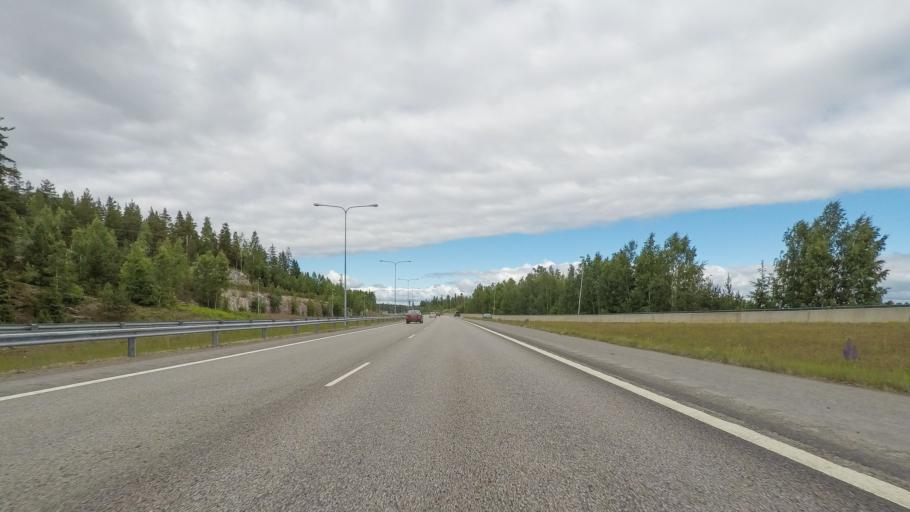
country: FI
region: Paijanne Tavastia
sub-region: Lahti
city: Heinola
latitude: 61.1947
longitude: 26.0029
